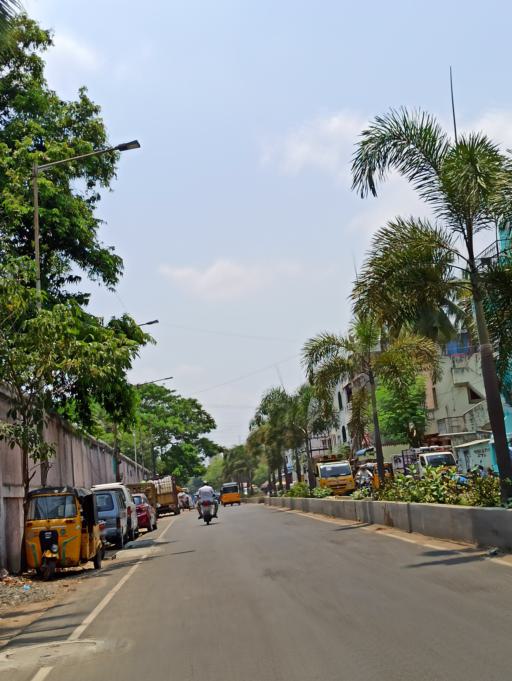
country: IN
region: Tamil Nadu
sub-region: Chennai
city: Chetput
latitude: 13.0927
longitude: 80.2375
